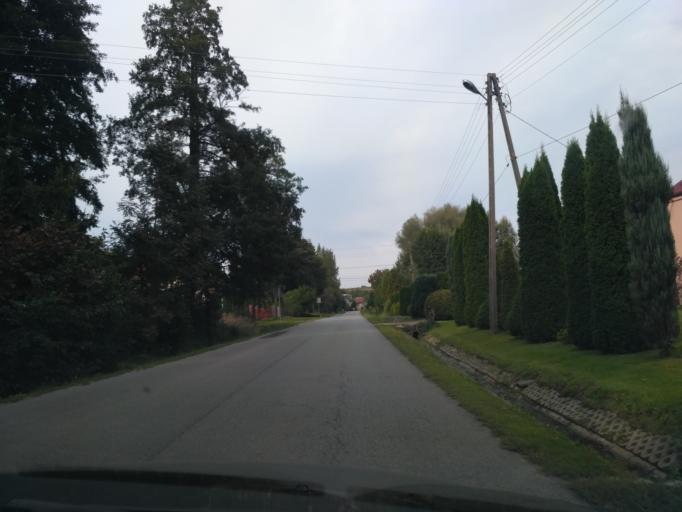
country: PL
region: Subcarpathian Voivodeship
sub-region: Powiat rzeszowski
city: Trzciana
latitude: 50.0426
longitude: 21.8335
